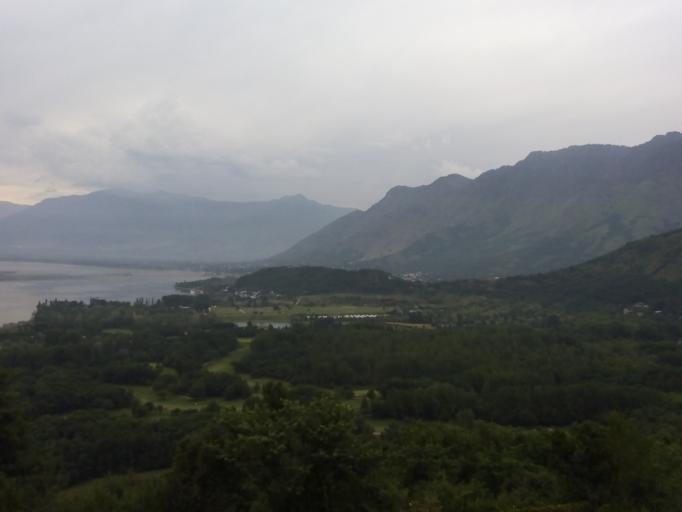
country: IN
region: Kashmir
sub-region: Srinagar
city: Srinagar
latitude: 34.0813
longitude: 74.8770
